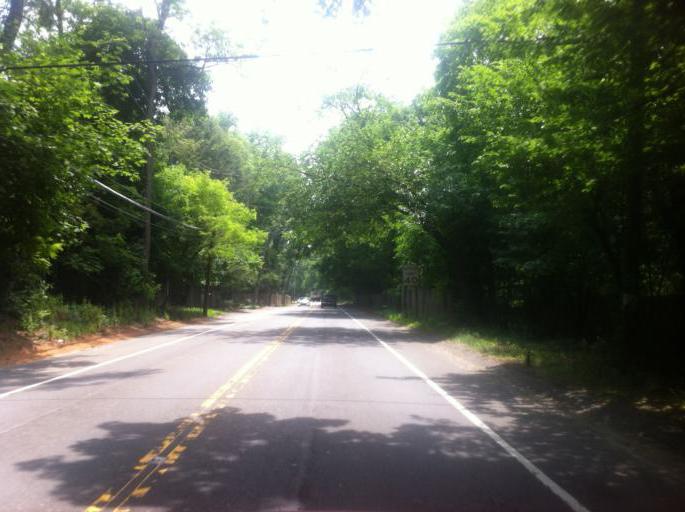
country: US
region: New York
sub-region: Nassau County
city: Old Brookville
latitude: 40.8366
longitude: -73.6127
